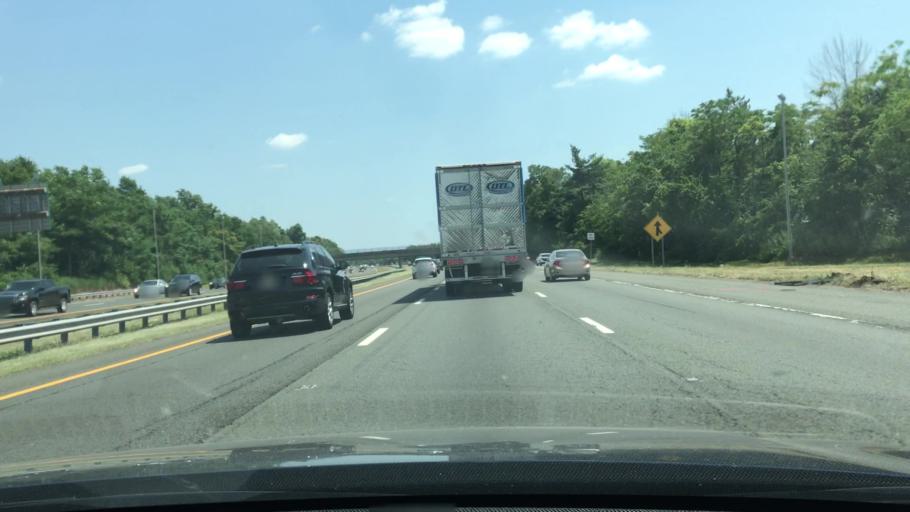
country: US
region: New Jersey
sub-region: Somerset County
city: South Bound Brook
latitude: 40.5496
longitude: -74.5408
